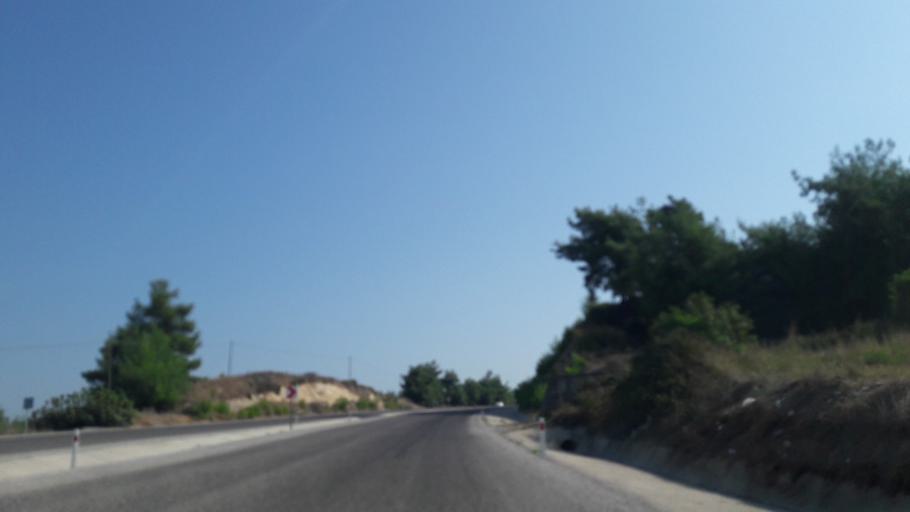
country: TR
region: Adana
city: Sagkaya
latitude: 37.1783
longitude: 35.5673
